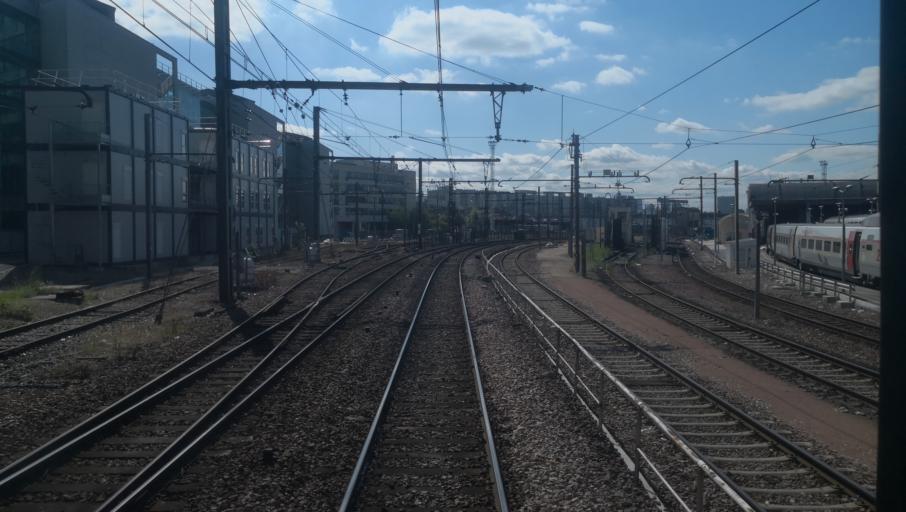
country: FR
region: Ile-de-France
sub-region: Departement du Val-de-Marne
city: Charenton-le-Pont
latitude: 48.8250
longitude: 2.4028
